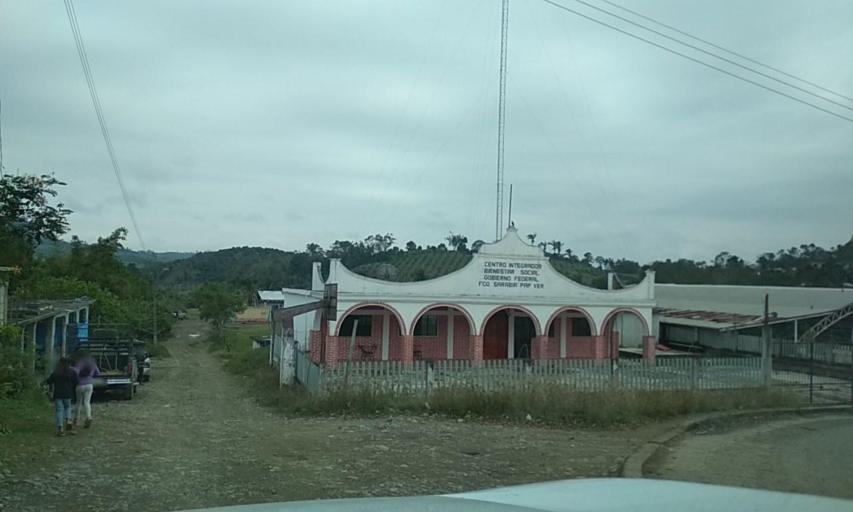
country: MX
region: Veracruz
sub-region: Coatzintla
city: Manuel Maria Contreras
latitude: 20.3595
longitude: -97.5106
